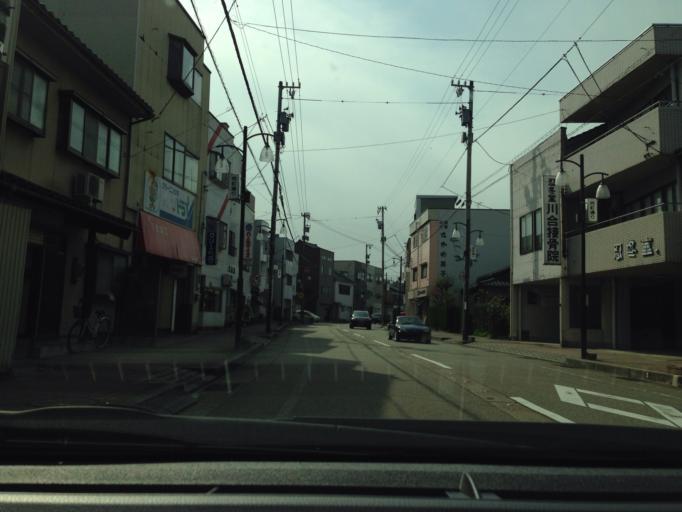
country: JP
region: Toyama
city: Fukumitsu
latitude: 36.5608
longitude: 136.8707
